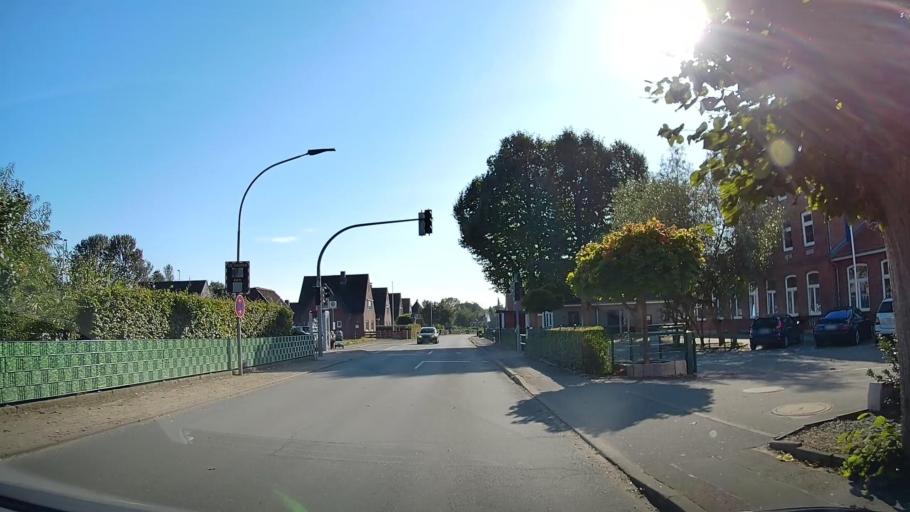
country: DE
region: Schleswig-Holstein
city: Fehmarn
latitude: 54.4490
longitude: 11.1447
